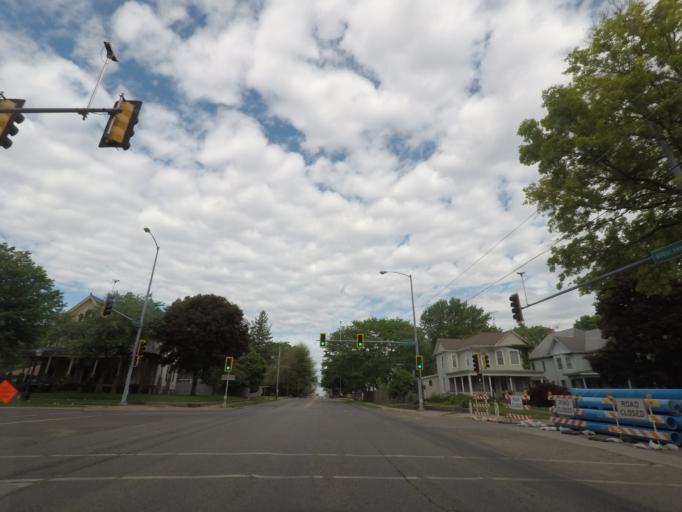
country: US
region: Illinois
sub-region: Logan County
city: Lincoln
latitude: 40.1576
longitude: -89.3677
